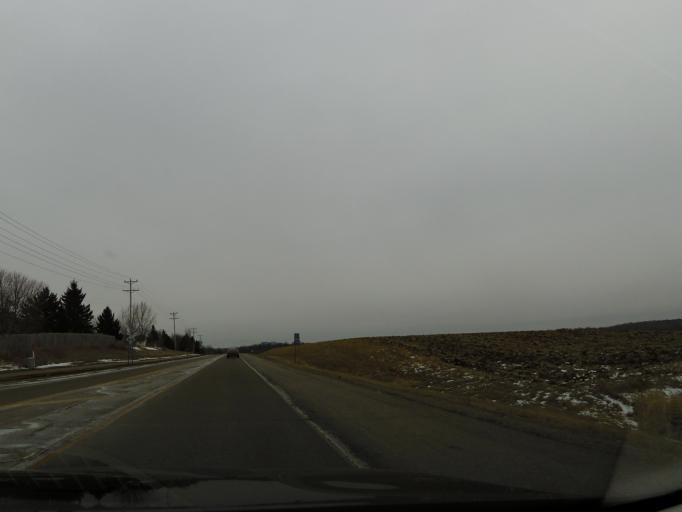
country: US
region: Minnesota
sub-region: Carver County
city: Waconia
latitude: 44.8317
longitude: -93.7884
